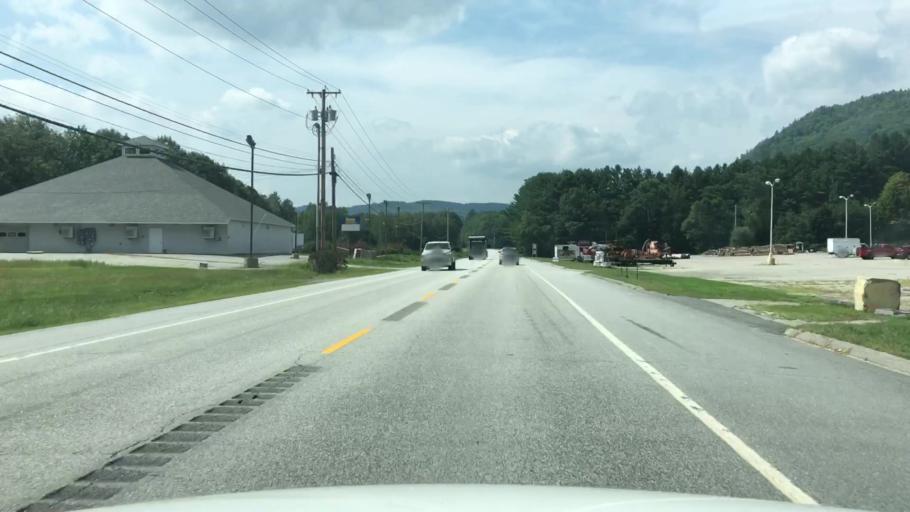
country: US
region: Maine
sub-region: Oxford County
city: Rumford
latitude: 44.5095
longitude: -70.5830
